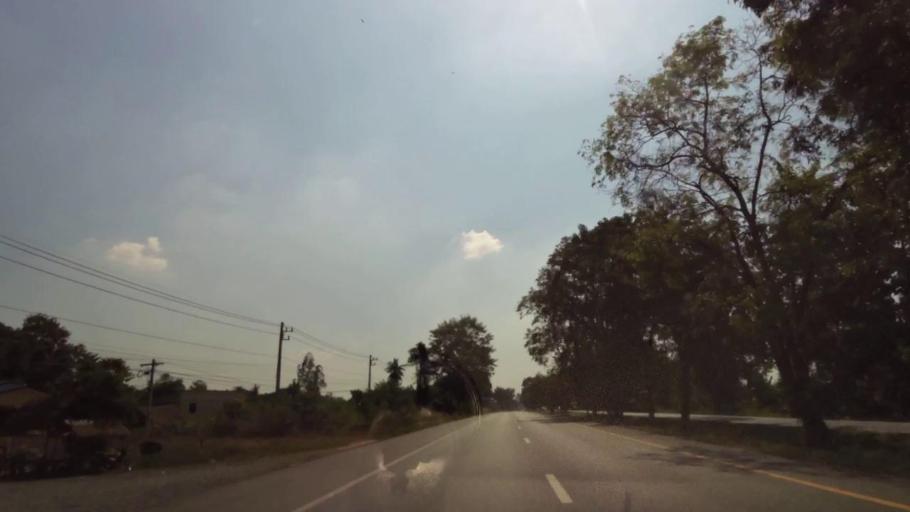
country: TH
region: Phichit
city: Bueng Na Rang
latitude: 16.1802
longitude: 100.1284
